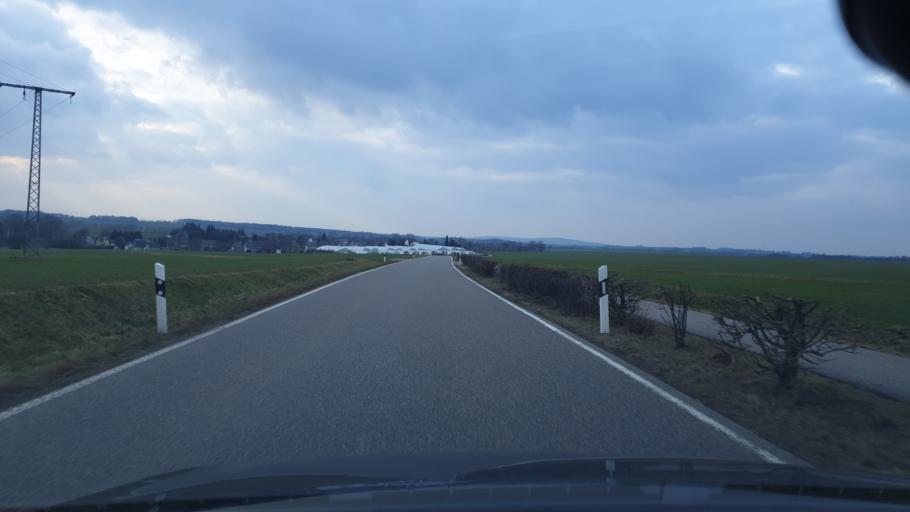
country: DE
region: Saxony
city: Altmittweida
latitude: 50.9868
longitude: 12.9402
